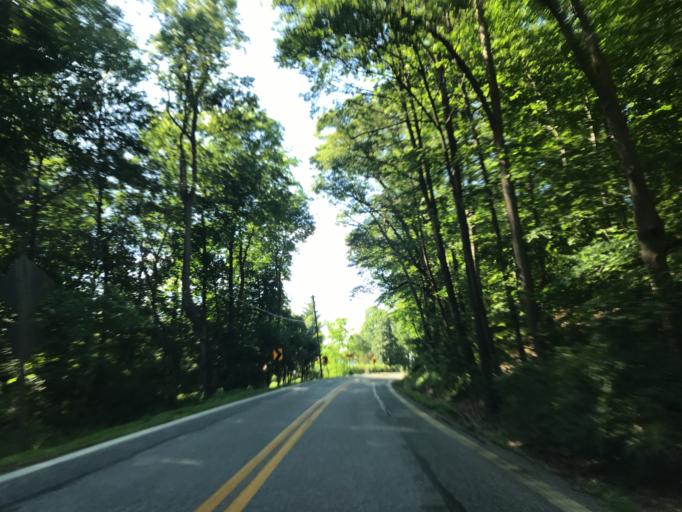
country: US
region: Maryland
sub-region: Baltimore County
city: Owings Mills
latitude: 39.4665
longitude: -76.7618
